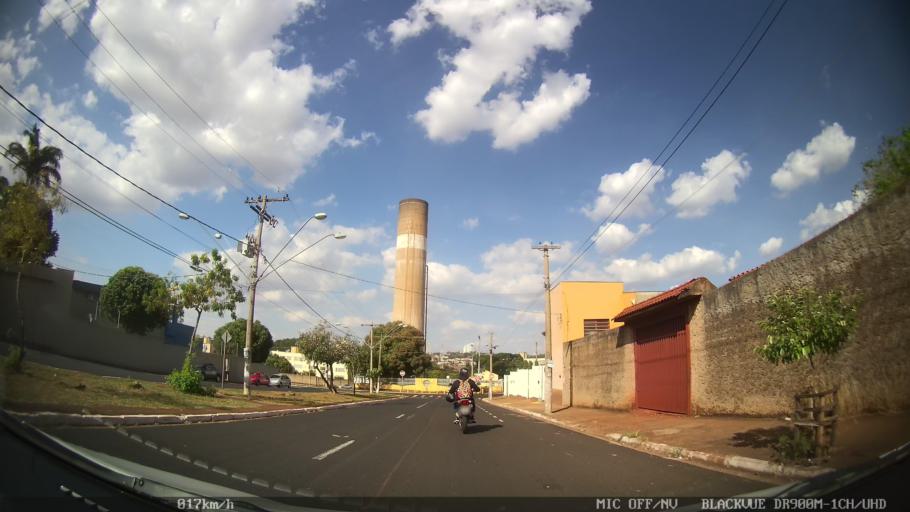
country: BR
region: Sao Paulo
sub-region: Ribeirao Preto
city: Ribeirao Preto
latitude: -21.1896
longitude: -47.8273
